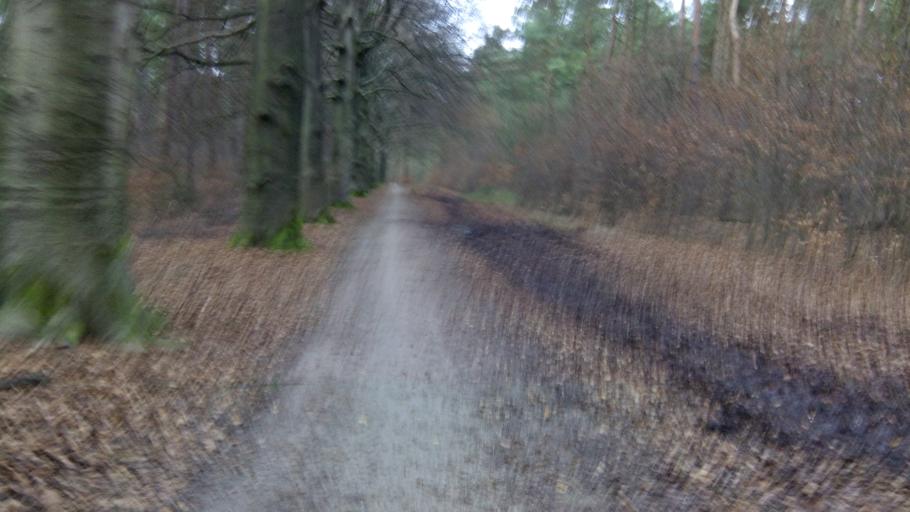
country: NL
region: North Holland
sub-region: Gemeente Hilversum
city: Hilversum
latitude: 52.1890
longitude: 5.2158
